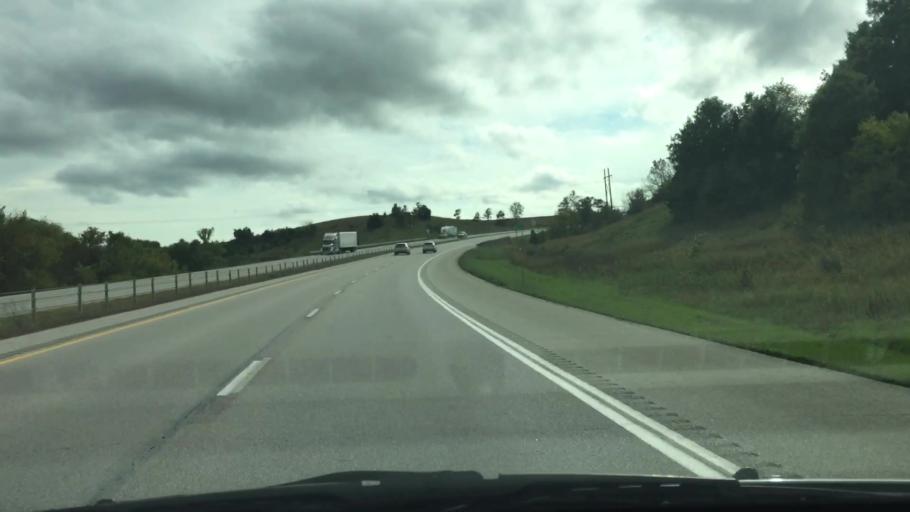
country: US
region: Iowa
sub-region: Clarke County
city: Osceola
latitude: 41.0542
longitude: -93.7821
